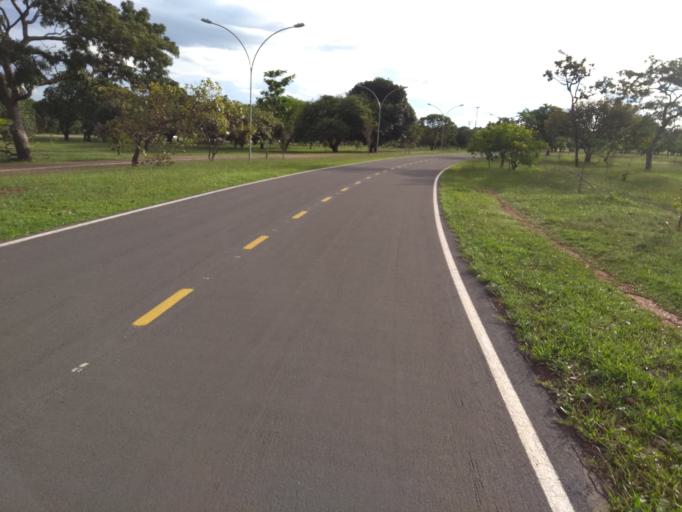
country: BR
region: Federal District
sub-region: Brasilia
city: Brasilia
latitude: -15.8111
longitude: -47.9210
